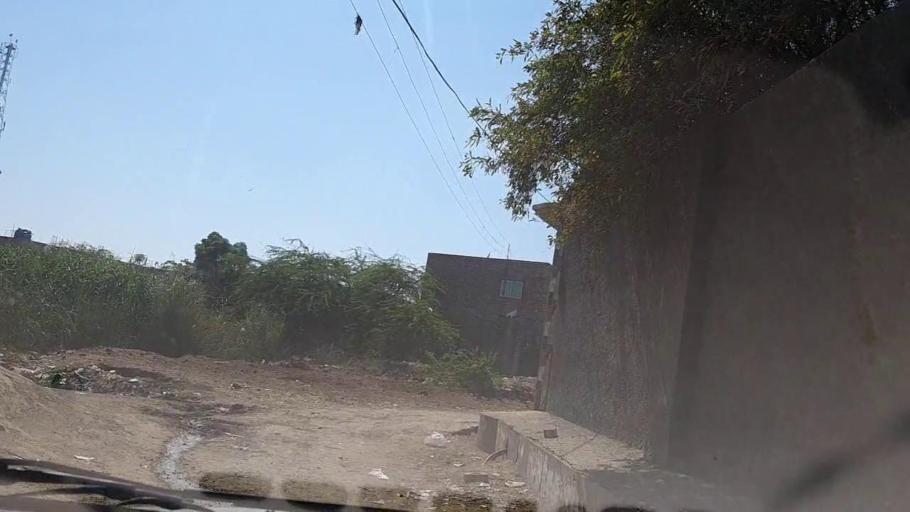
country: PK
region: Sindh
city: Mirpur Khas
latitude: 25.4340
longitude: 69.0190
